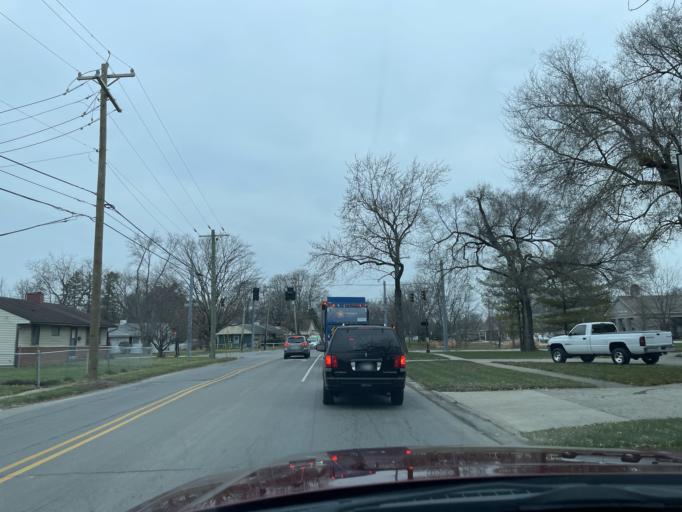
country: US
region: Indiana
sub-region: Hendricks County
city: Brownsburg
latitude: 39.8355
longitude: -86.4013
